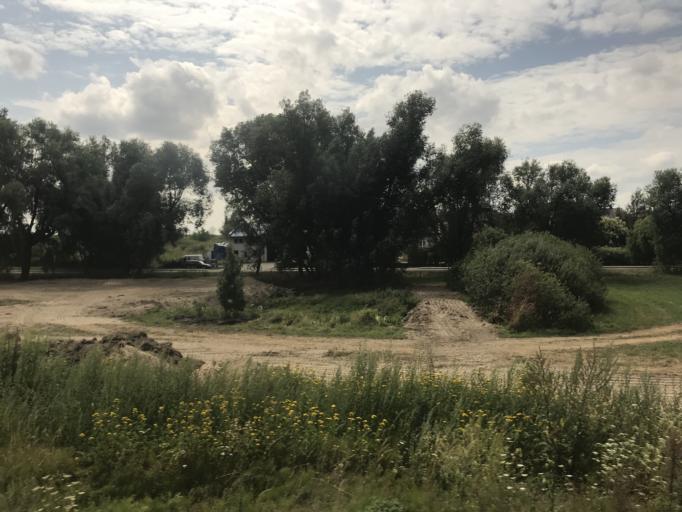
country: PL
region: Greater Poland Voivodeship
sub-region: Powiat poznanski
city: Pobiedziska
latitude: 52.4755
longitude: 17.2507
